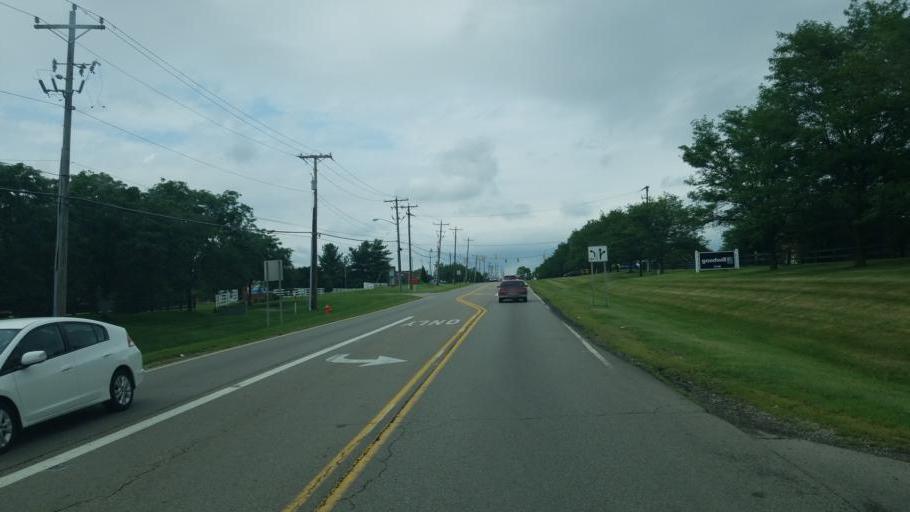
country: US
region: Ohio
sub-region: Franklin County
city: Gahanna
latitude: 40.0602
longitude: -82.8633
